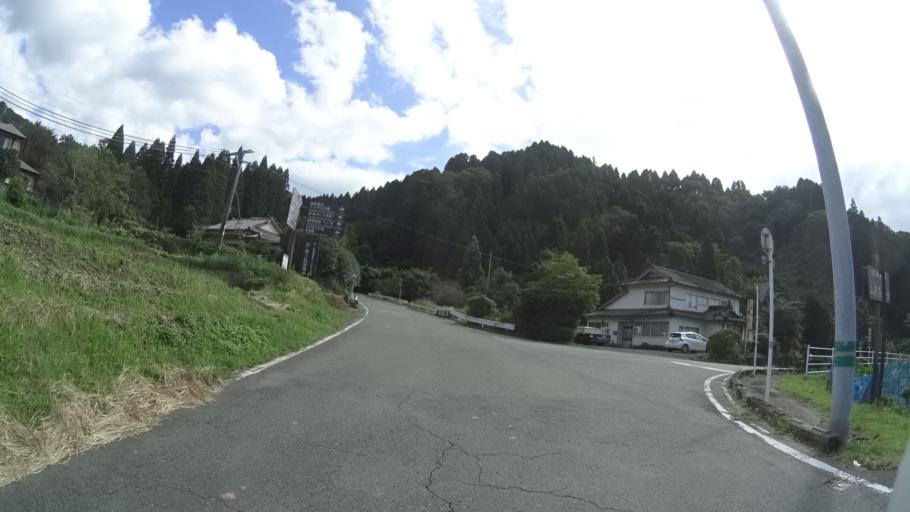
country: JP
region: Kumamoto
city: Aso
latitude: 32.8133
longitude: 131.1309
